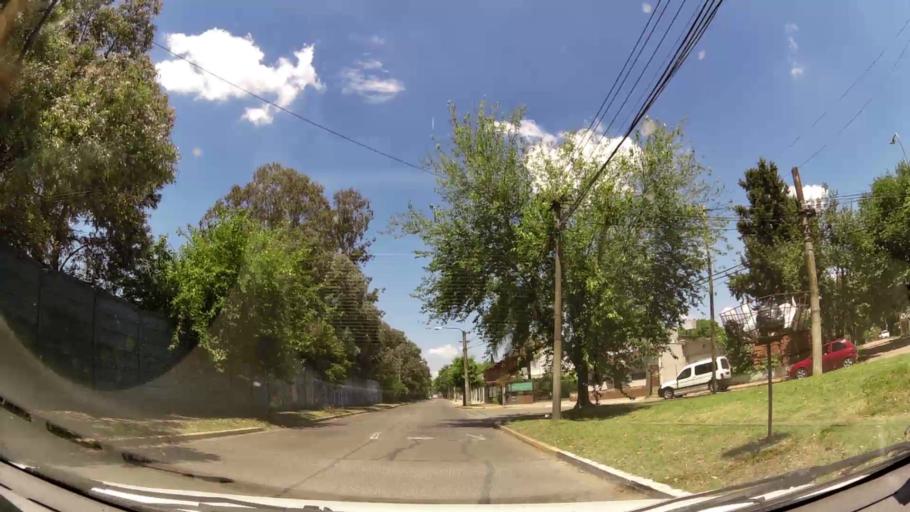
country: AR
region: Buenos Aires
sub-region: Partido de Merlo
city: Merlo
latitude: -34.6611
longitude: -58.7060
